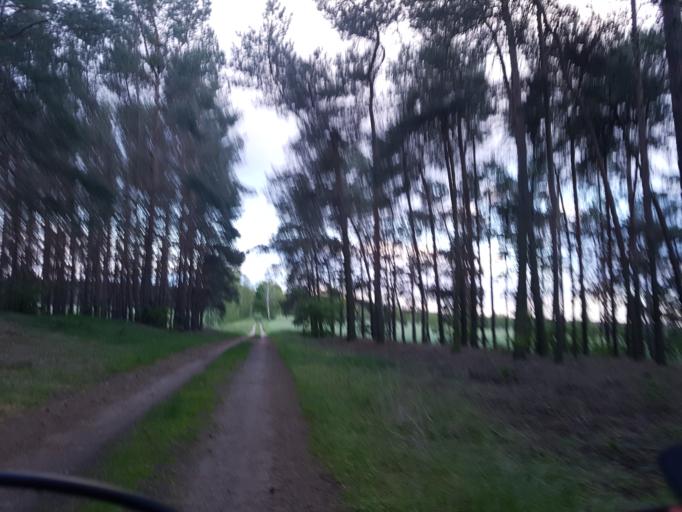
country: DE
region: Brandenburg
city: Schilda
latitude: 51.5707
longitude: 13.3732
